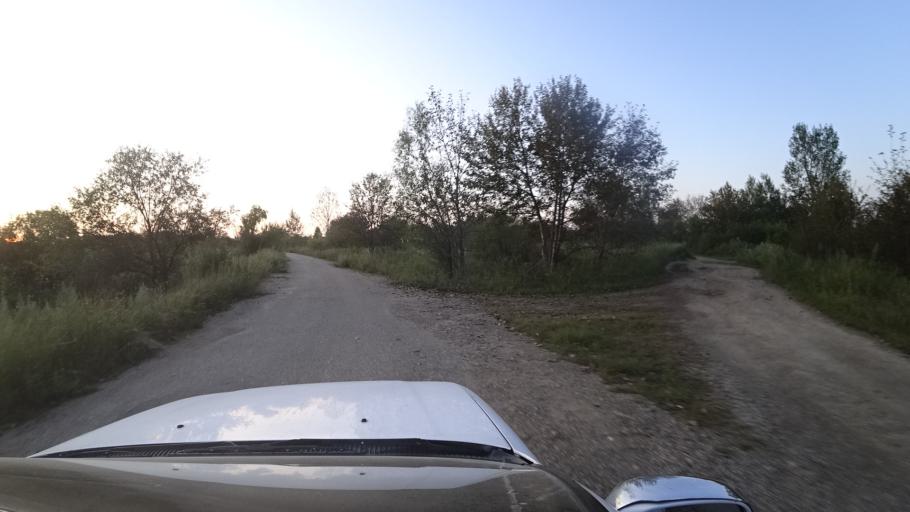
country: RU
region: Primorskiy
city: Dal'nerechensk
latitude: 45.9486
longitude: 133.7622
